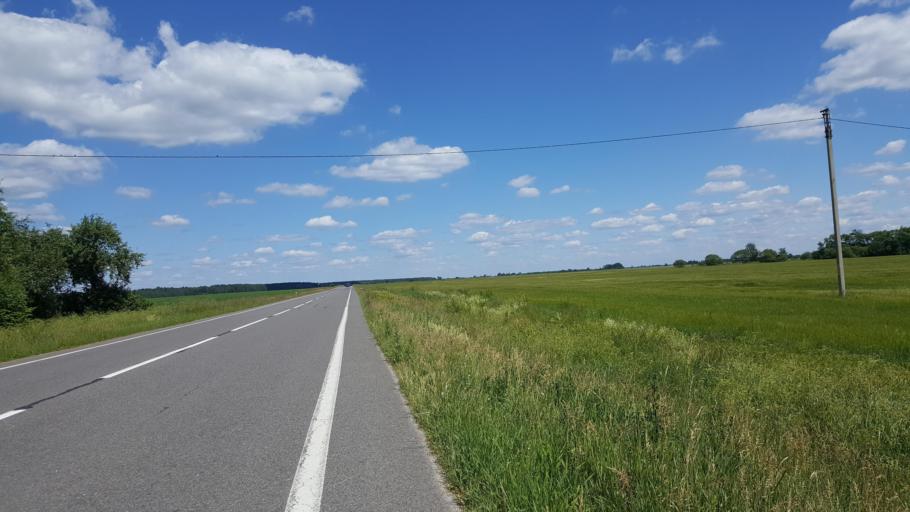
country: PL
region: Podlasie
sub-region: Powiat hajnowski
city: Czeremcha
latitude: 52.5044
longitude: 23.5052
